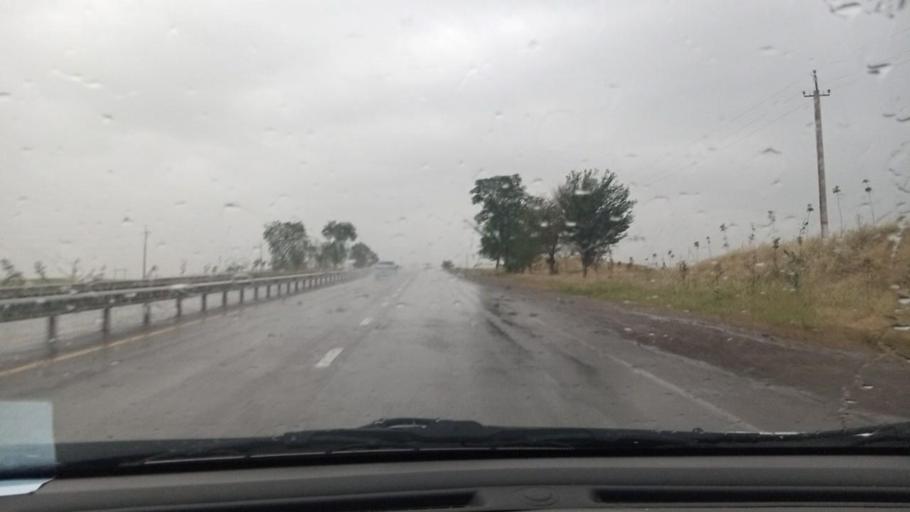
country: UZ
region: Toshkent
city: Ohangaron
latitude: 40.9506
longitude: 69.5703
